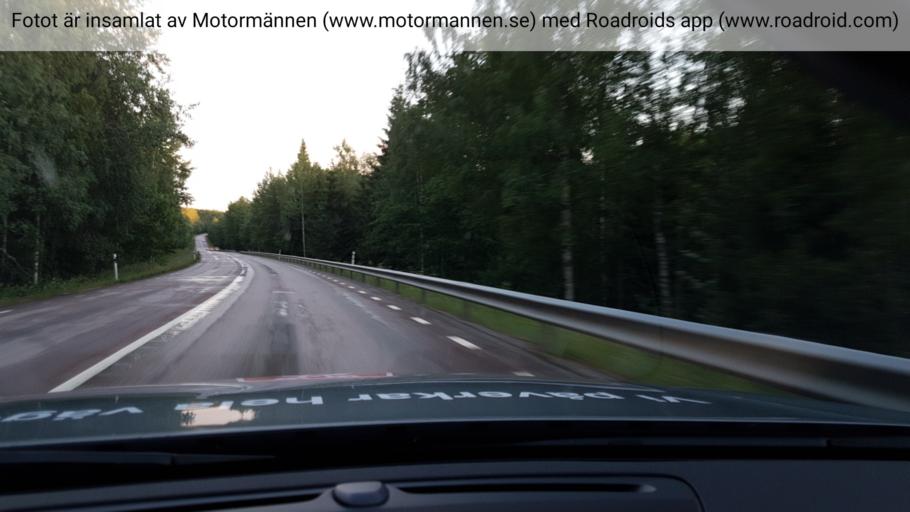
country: SE
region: Vaestmanland
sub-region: Fagersta Kommun
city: Fagersta
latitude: 59.9390
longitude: 15.7314
